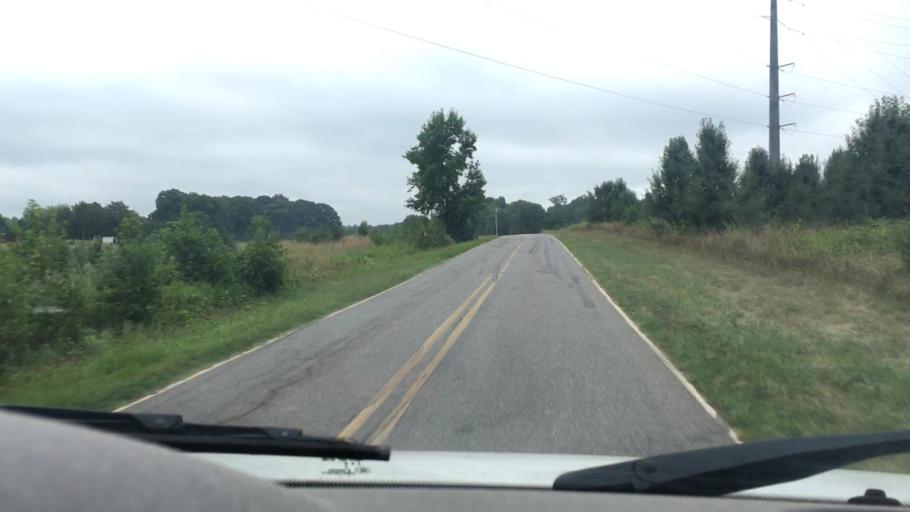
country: US
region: North Carolina
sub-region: Gaston County
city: Davidson
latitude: 35.5329
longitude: -80.8302
